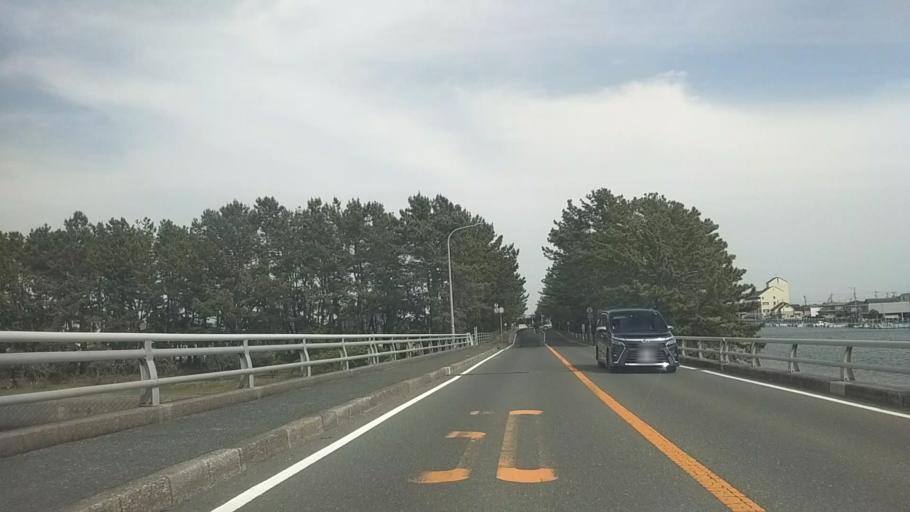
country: JP
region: Shizuoka
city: Kosai-shi
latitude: 34.6979
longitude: 137.6033
